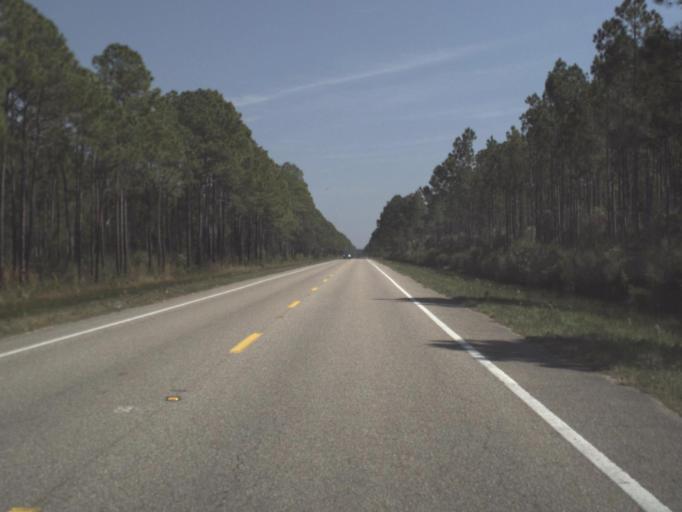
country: US
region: Florida
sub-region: Franklin County
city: Apalachicola
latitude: 29.7304
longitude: -85.1391
